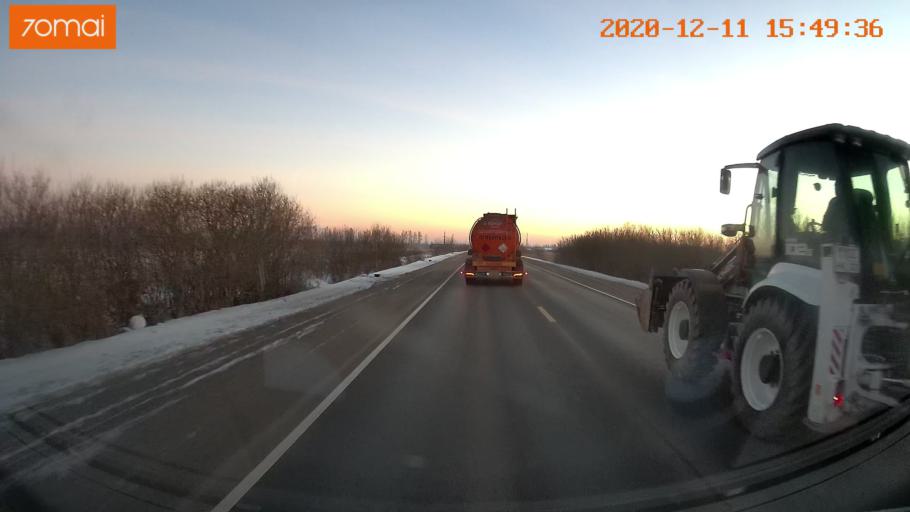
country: RU
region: Ivanovo
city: Novo-Talitsy
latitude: 56.9868
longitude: 40.8758
